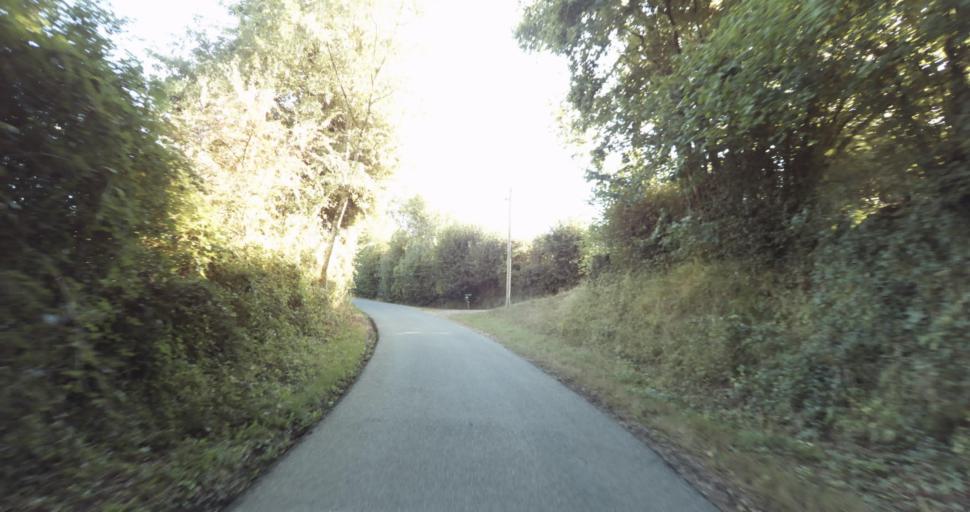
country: FR
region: Lower Normandy
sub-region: Departement de l'Orne
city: Vimoutiers
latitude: 48.8914
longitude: 0.1313
